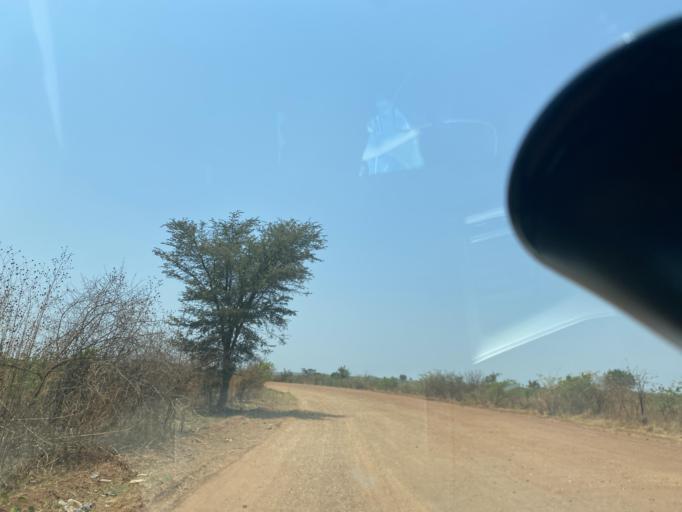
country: ZM
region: Lusaka
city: Lusaka
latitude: -15.4606
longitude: 27.9192
